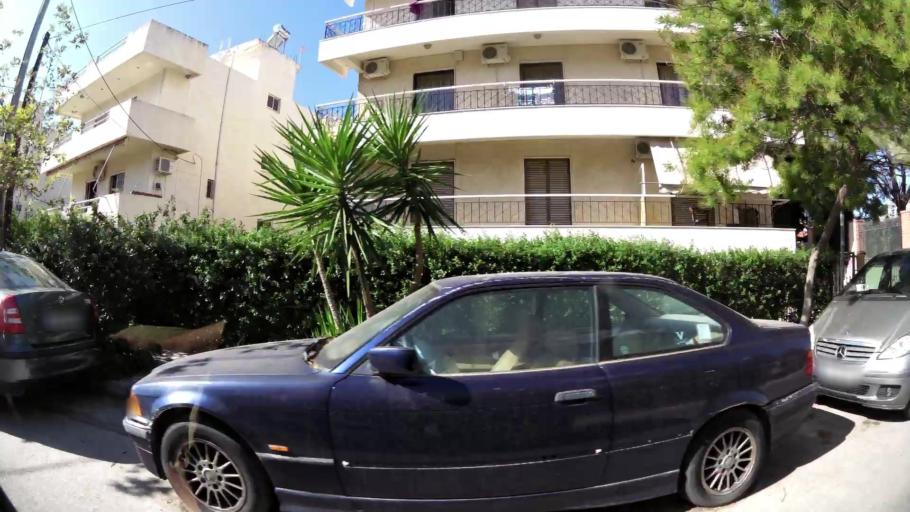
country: GR
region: Attica
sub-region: Nomarchia Anatolikis Attikis
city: Voula
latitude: 37.8320
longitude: 23.7760
